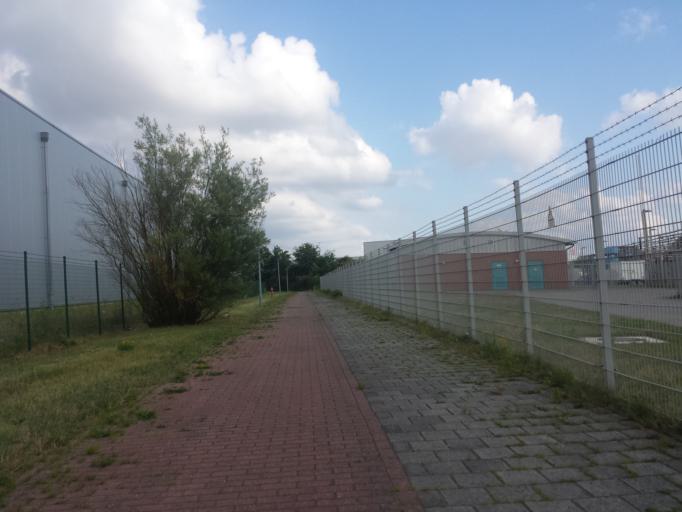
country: DE
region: Lower Saxony
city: Delmenhorst
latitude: 53.0935
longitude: 8.6951
